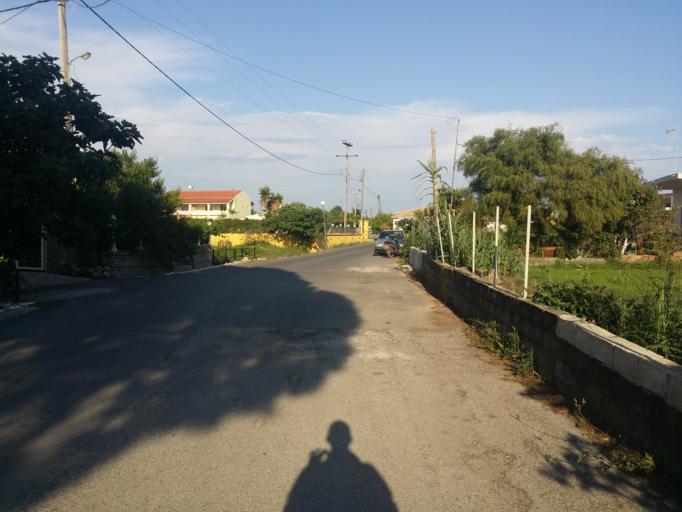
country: GR
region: Ionian Islands
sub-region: Nomos Kerkyras
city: Perivoli
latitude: 39.4282
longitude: 19.9478
